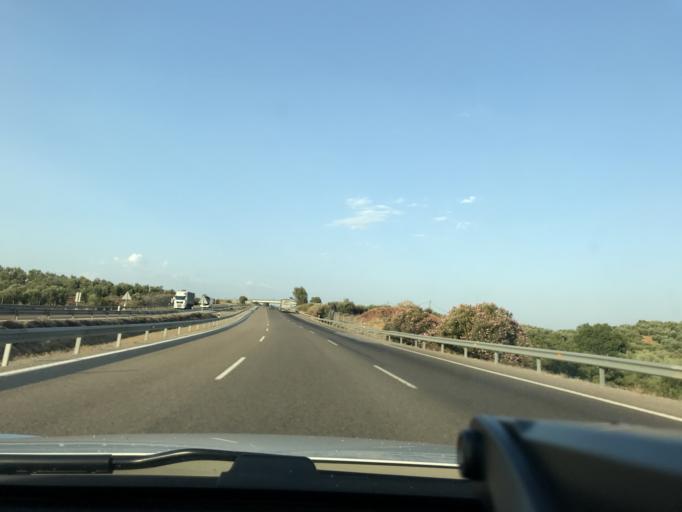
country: ES
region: Andalusia
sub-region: Provincia de Jaen
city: Bailen
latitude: 38.0873
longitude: -3.8249
